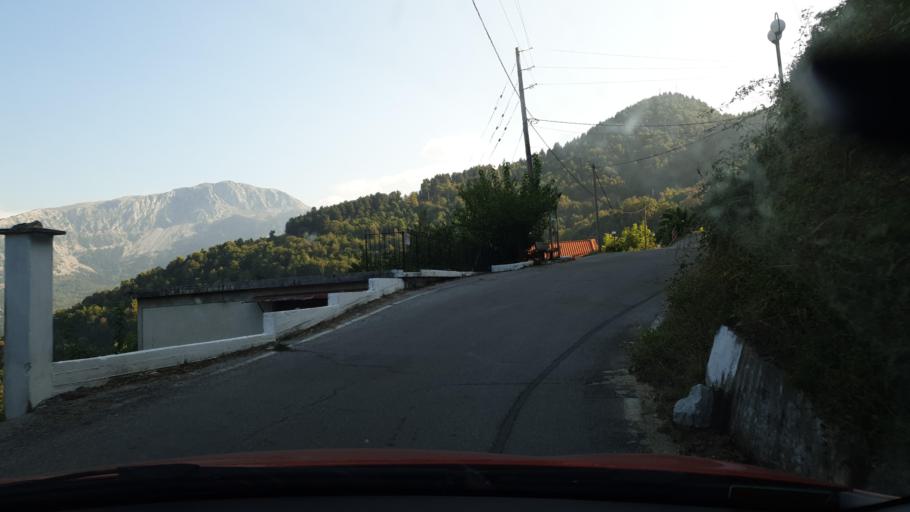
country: GR
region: Central Greece
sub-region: Nomos Evvoias
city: Kymi
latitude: 38.6420
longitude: 23.9377
